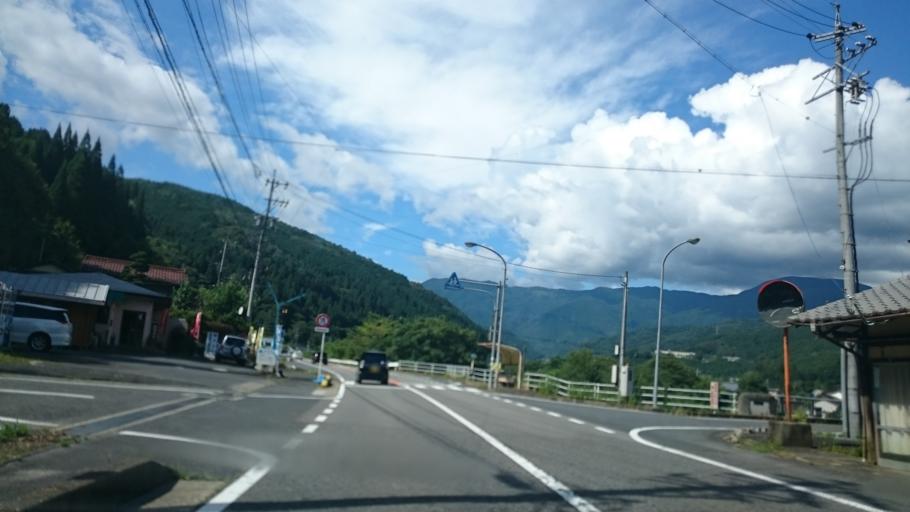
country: JP
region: Gifu
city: Nakatsugawa
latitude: 35.6118
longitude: 137.4598
